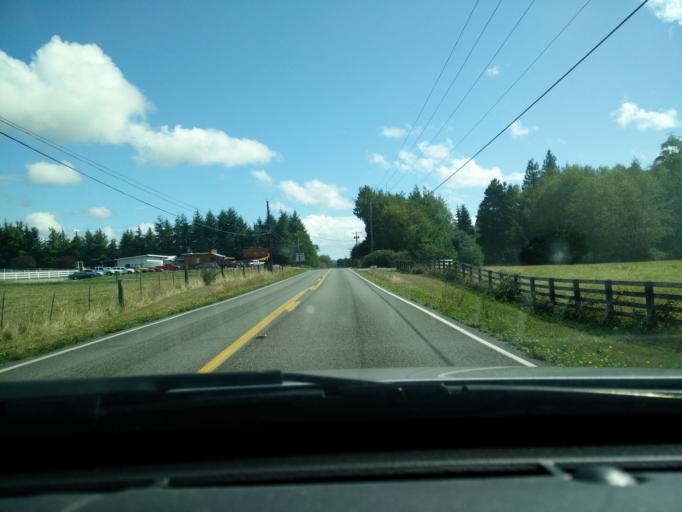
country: US
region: Washington
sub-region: Snohomish County
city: Stanwood
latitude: 48.2685
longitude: -122.3333
